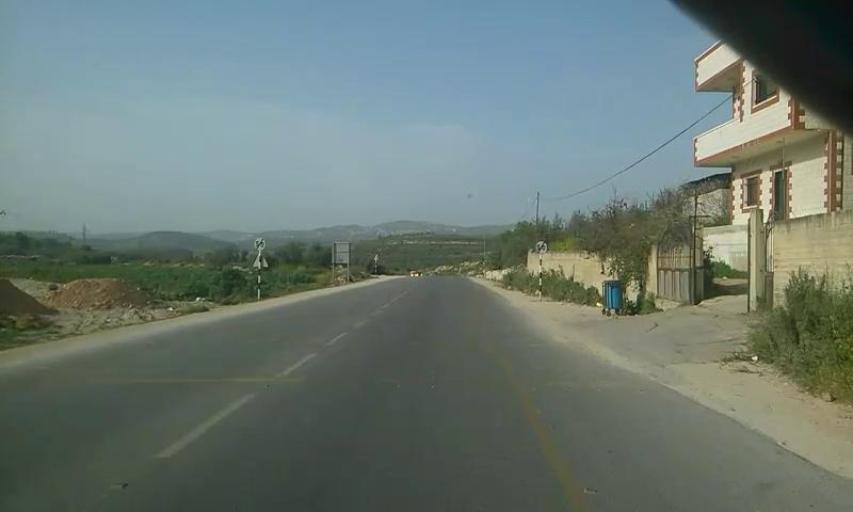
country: PS
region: West Bank
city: Dayr Sharaf
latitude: 32.2548
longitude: 35.1776
